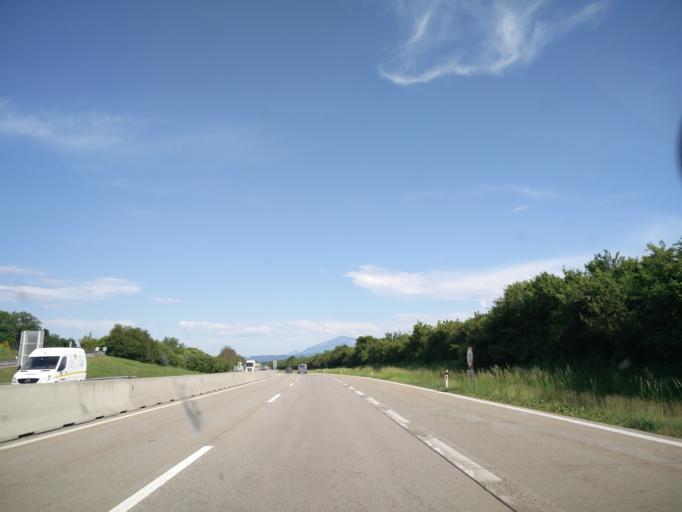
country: AT
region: Carinthia
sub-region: Klagenfurt am Woerthersee
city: Klagenfurt am Woerthersee
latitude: 46.6461
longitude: 14.3353
